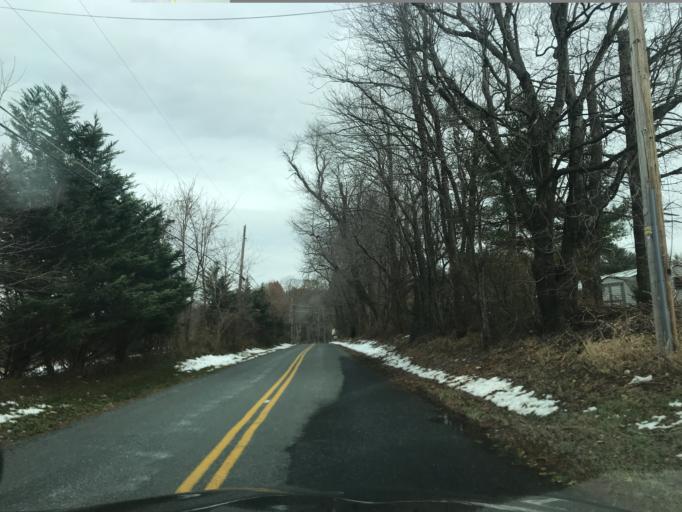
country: US
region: Pennsylvania
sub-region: York County
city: Susquehanna Trails
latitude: 39.6858
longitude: -76.4220
